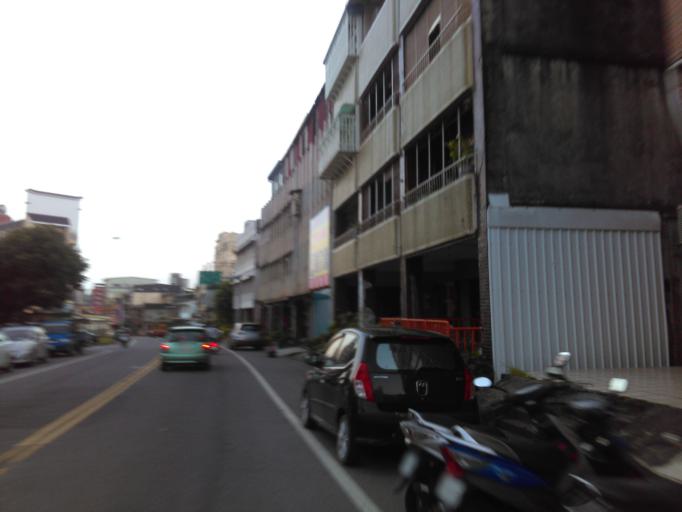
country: TW
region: Taiwan
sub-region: Yilan
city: Yilan
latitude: 24.8201
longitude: 121.7670
